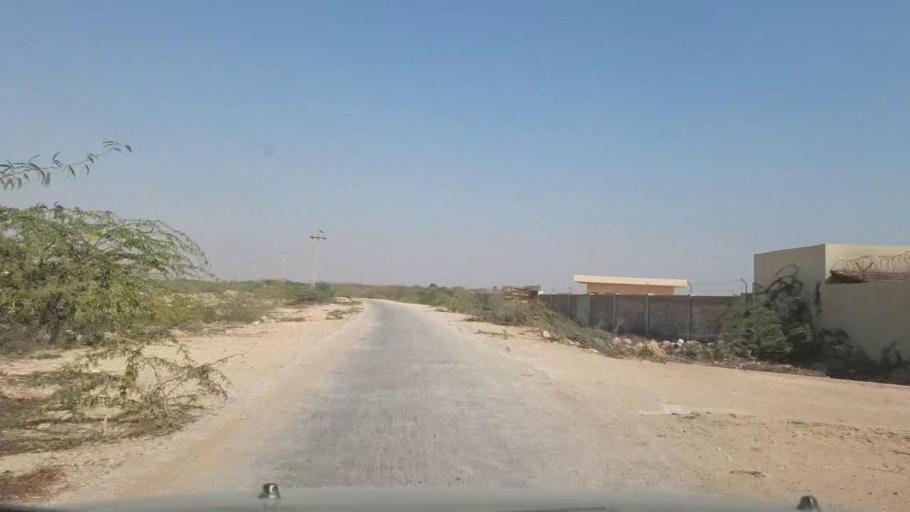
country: PK
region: Sindh
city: Thatta
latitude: 24.9961
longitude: 68.0097
